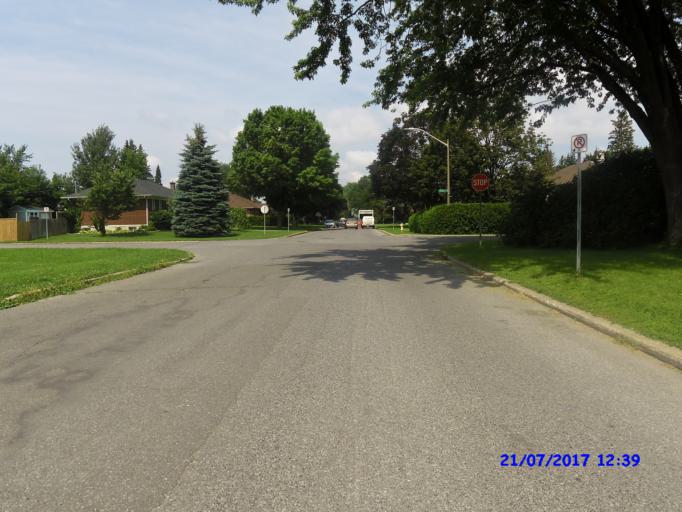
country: CA
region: Ontario
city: Ottawa
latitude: 45.3662
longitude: -75.7210
